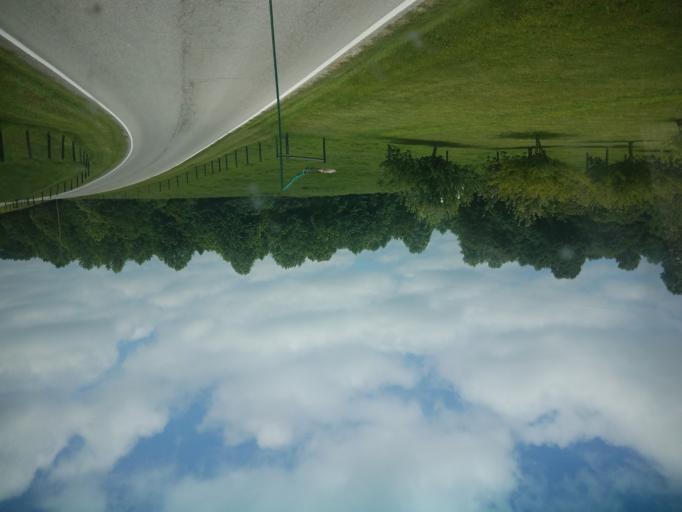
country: US
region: Kentucky
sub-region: Hart County
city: Munfordville
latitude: 37.3452
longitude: -86.0372
